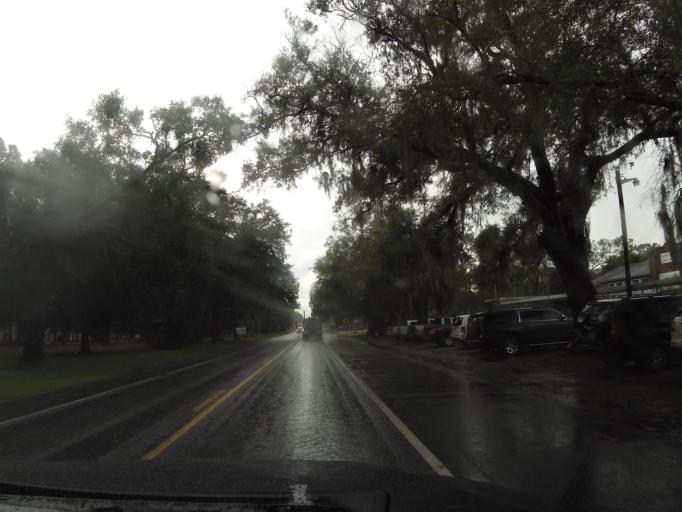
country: US
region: Florida
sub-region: Nassau County
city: Hilliard
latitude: 30.5255
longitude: -82.0381
